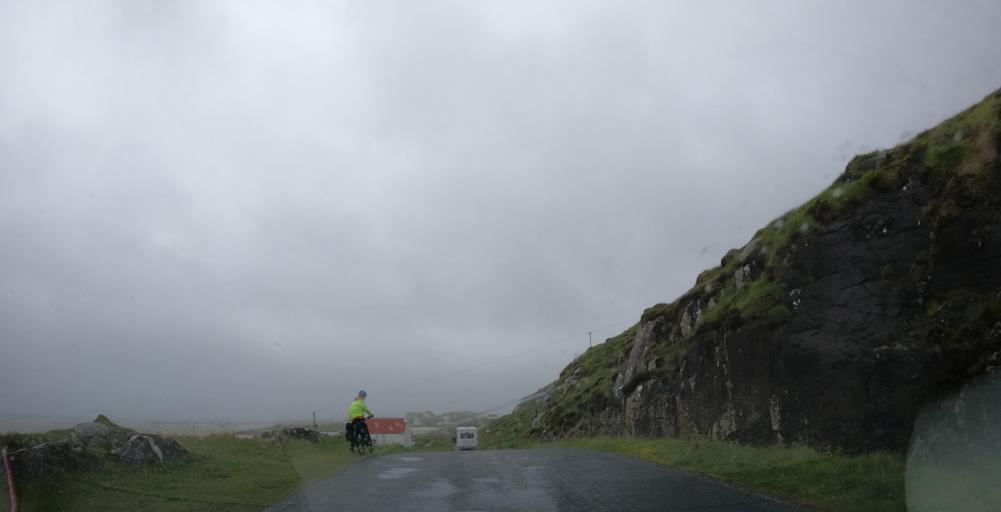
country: GB
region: Scotland
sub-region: Eilean Siar
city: Barra
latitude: 57.0172
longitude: -7.4367
